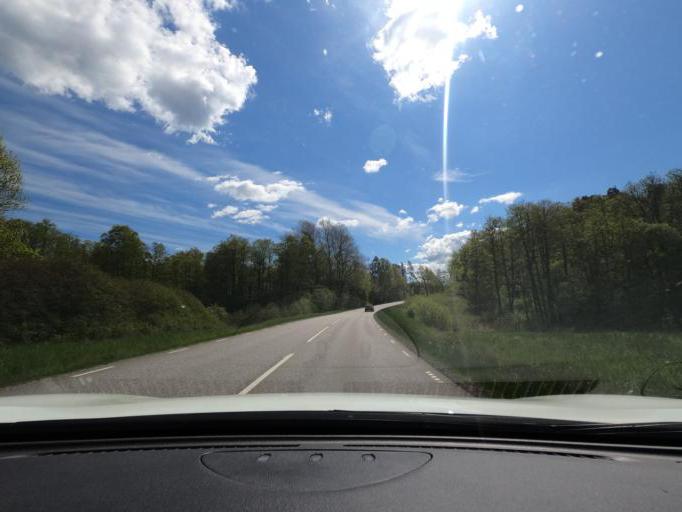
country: SE
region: Halland
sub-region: Kungsbacka Kommun
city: Fjaeras kyrkby
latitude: 57.4170
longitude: 12.2099
